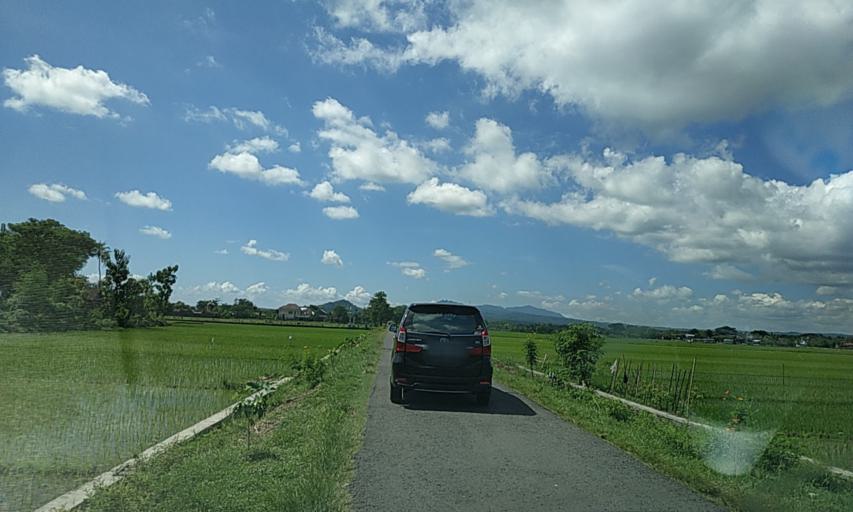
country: ID
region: Central Java
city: Trucuk
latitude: -7.7441
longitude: 110.7327
